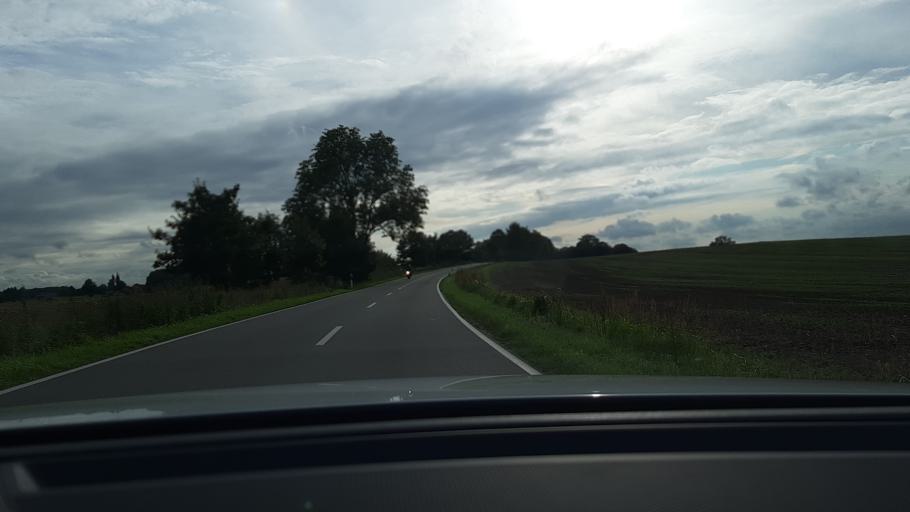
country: DE
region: Schleswig-Holstein
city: Badendorf
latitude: 53.8599
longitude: 10.5498
